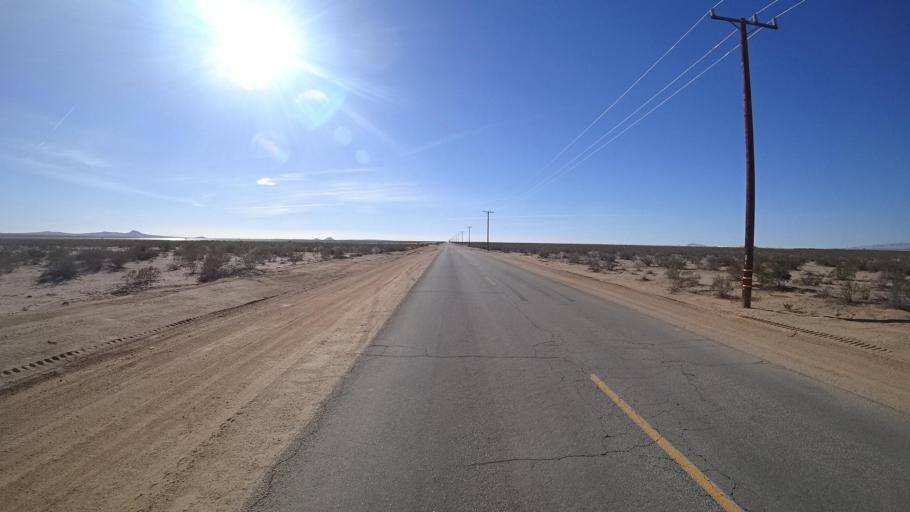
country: US
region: California
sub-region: Kern County
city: California City
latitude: 35.2017
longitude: -117.9858
